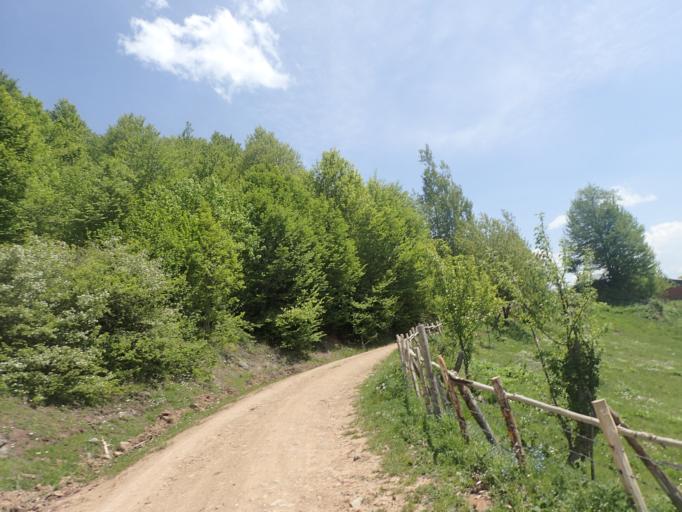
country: TR
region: Ordu
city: Akkus
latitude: 40.8206
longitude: 36.9511
